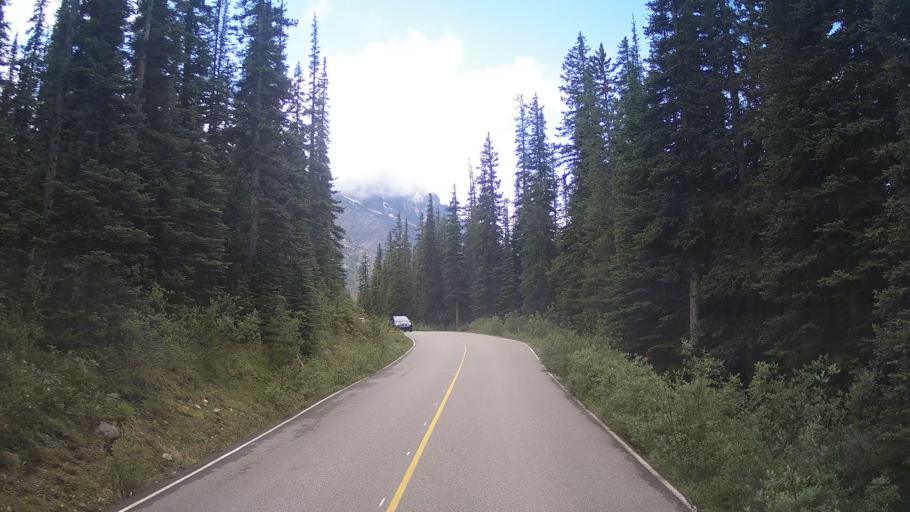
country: CA
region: Alberta
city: Jasper Park Lodge
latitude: 52.7171
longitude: -118.0542
